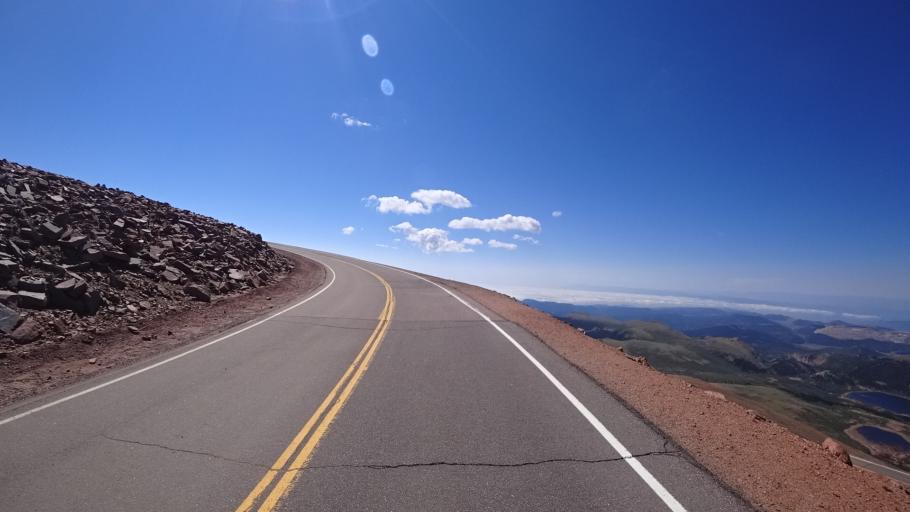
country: US
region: Colorado
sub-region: El Paso County
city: Cascade-Chipita Park
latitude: 38.8404
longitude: -105.0463
